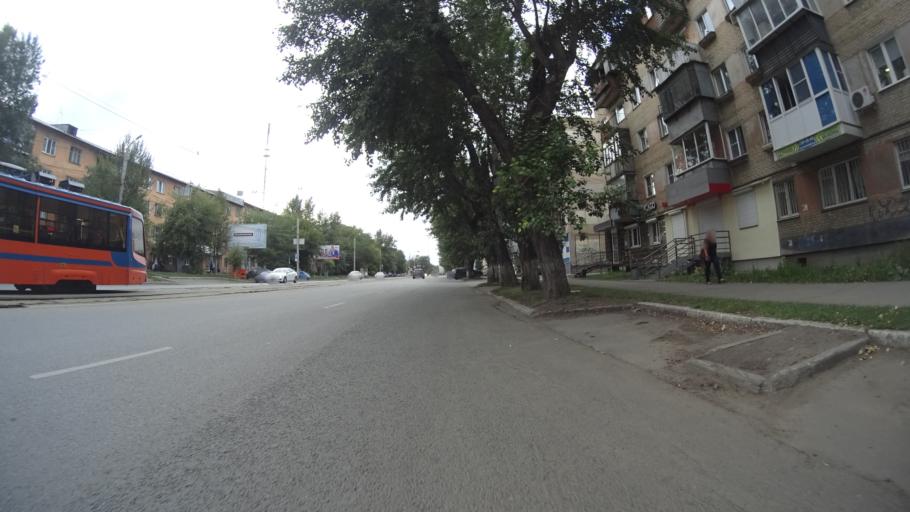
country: RU
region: Chelyabinsk
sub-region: Gorod Chelyabinsk
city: Chelyabinsk
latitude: 55.1511
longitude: 61.4112
